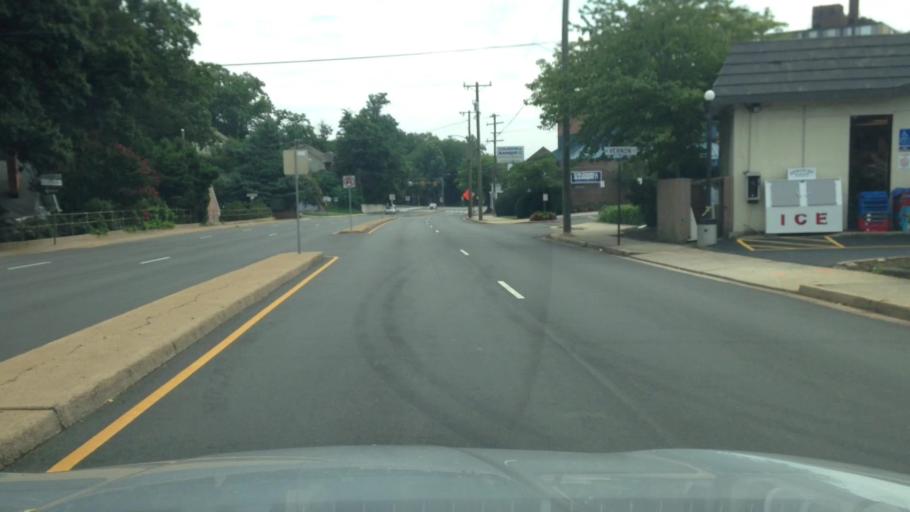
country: US
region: Virginia
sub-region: Arlington County
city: Arlington
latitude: 38.8989
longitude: -77.1191
